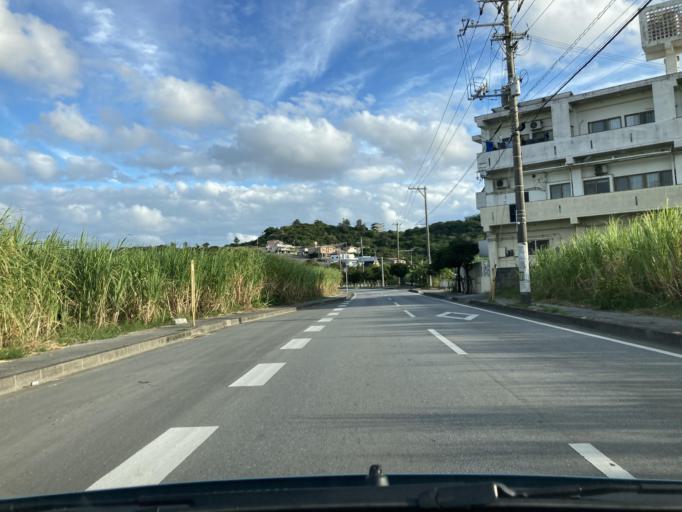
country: JP
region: Okinawa
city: Tomigusuku
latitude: 26.1521
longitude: 127.7430
